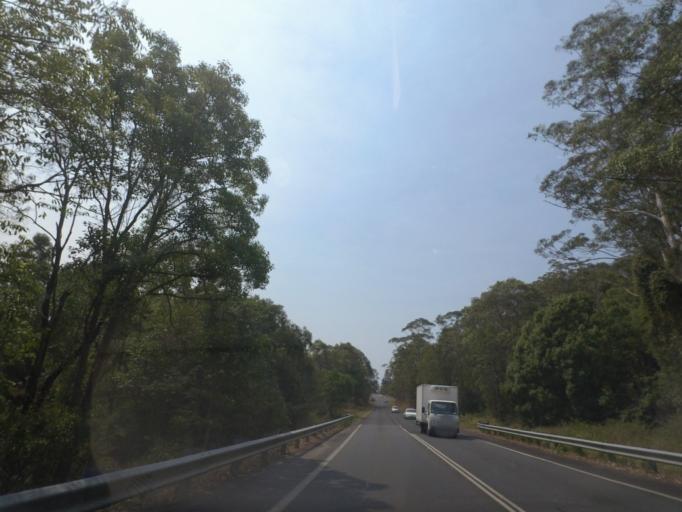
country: AU
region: New South Wales
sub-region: Byron Shire
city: Brunswick Heads
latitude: -28.4965
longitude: 153.5264
